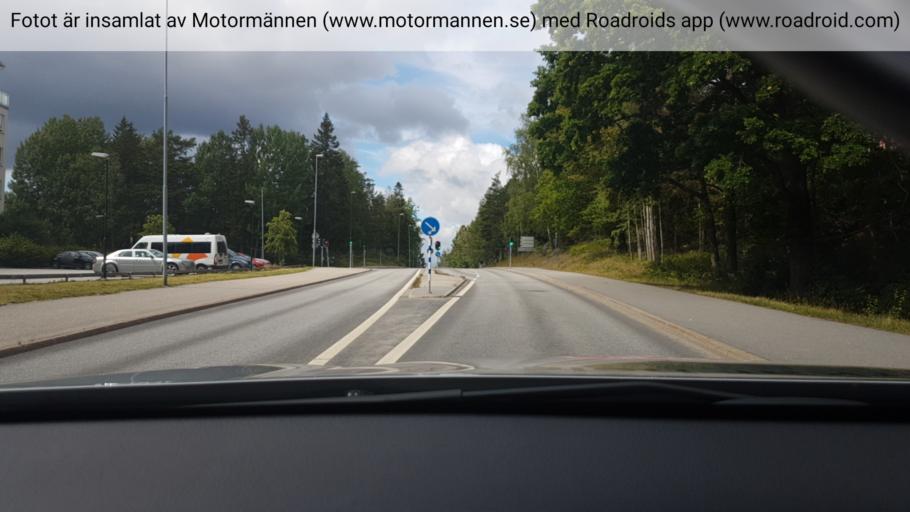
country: SE
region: Stockholm
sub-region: Tyreso Kommun
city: Bollmora
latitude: 59.2360
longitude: 18.2231
